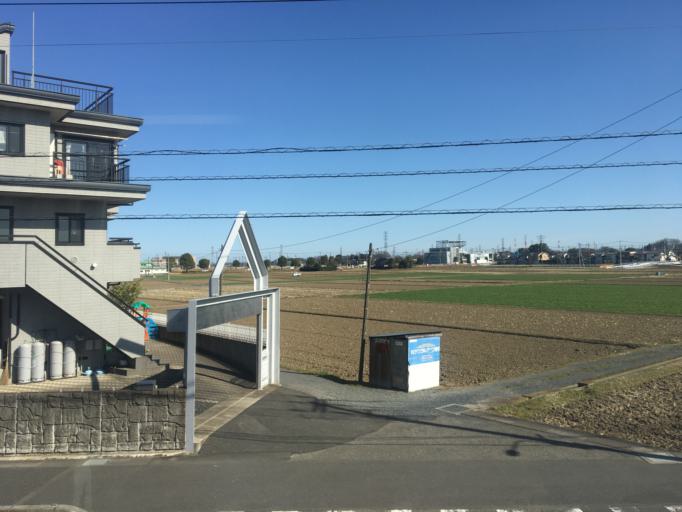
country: JP
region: Saitama
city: Sakado
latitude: 35.9798
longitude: 139.3998
